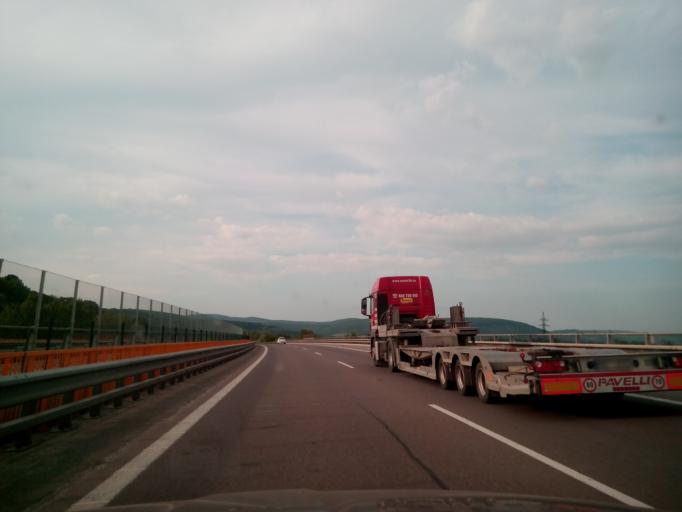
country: SK
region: Trenciansky
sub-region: Okres Trencin
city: Trencin
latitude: 48.8817
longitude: 17.9806
